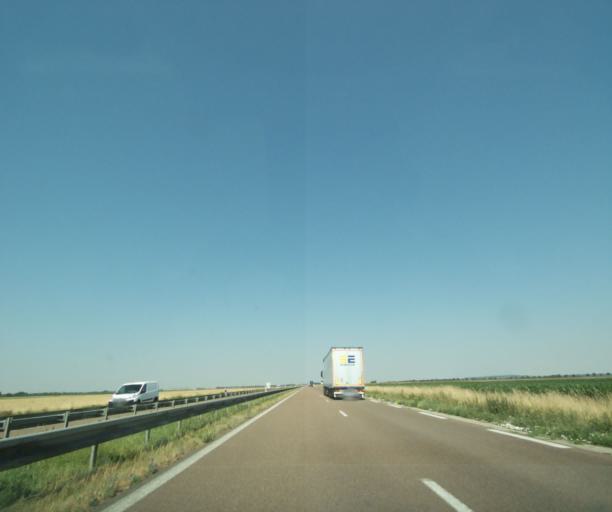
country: FR
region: Champagne-Ardenne
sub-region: Departement de la Marne
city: Frignicourt
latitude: 48.6954
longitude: 4.6970
